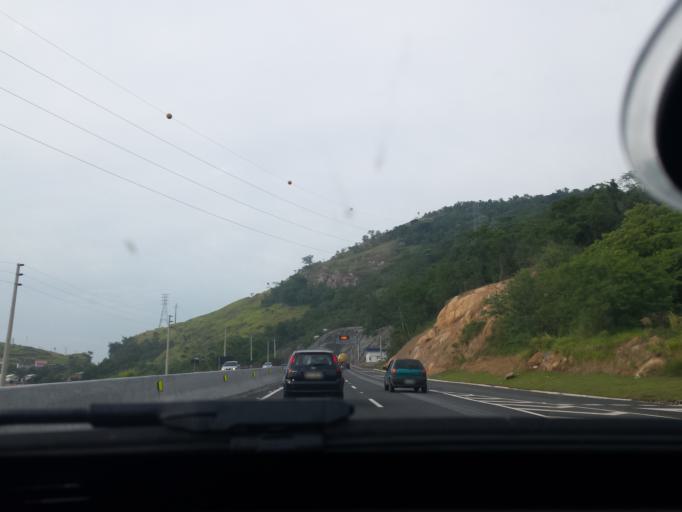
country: BR
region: Santa Catarina
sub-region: Tubarao
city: Tubarao
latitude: -28.4847
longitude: -49.0363
